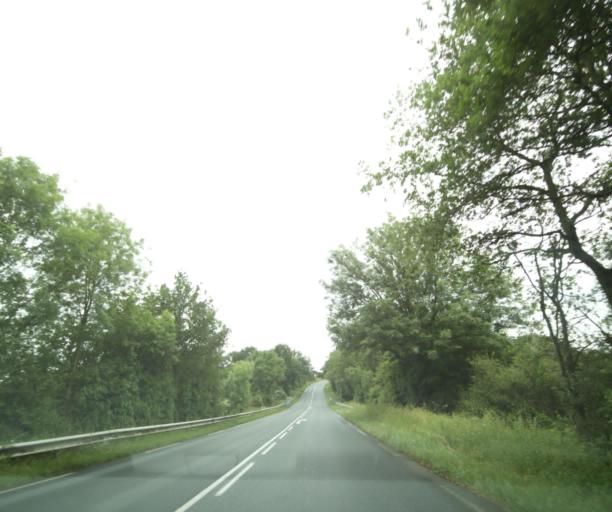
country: FR
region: Poitou-Charentes
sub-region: Departement des Deux-Sevres
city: Viennay
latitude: 46.7109
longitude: -0.2395
